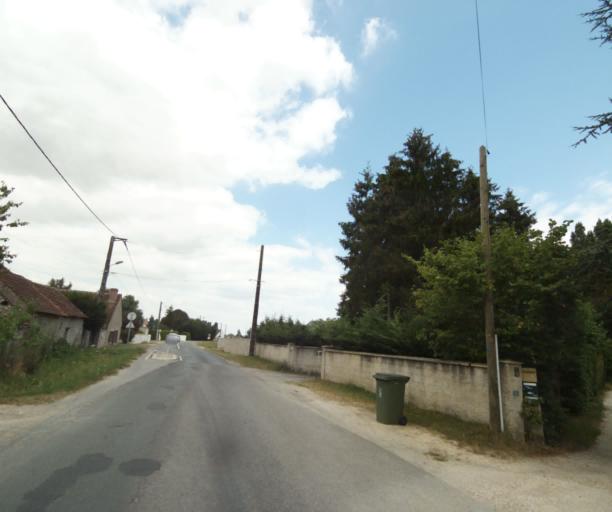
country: FR
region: Centre
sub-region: Departement du Loiret
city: Checy
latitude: 47.9161
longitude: 2.0405
